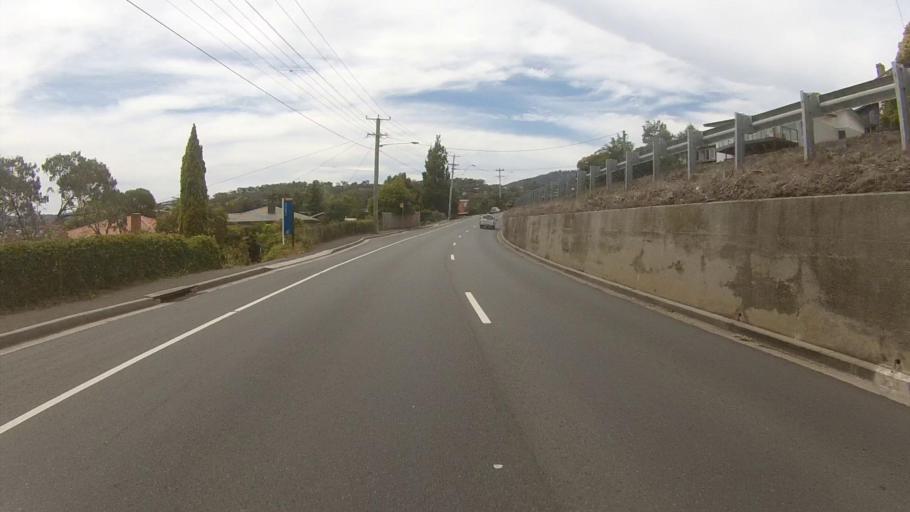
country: AU
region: Tasmania
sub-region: Clarence
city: Lindisfarne
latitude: -42.8540
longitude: 147.3571
